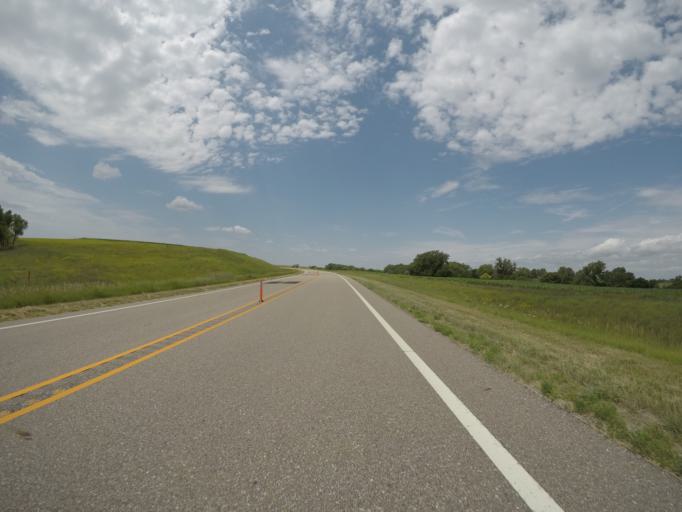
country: US
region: Kansas
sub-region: Graham County
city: Hill City
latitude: 39.3938
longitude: -99.6440
